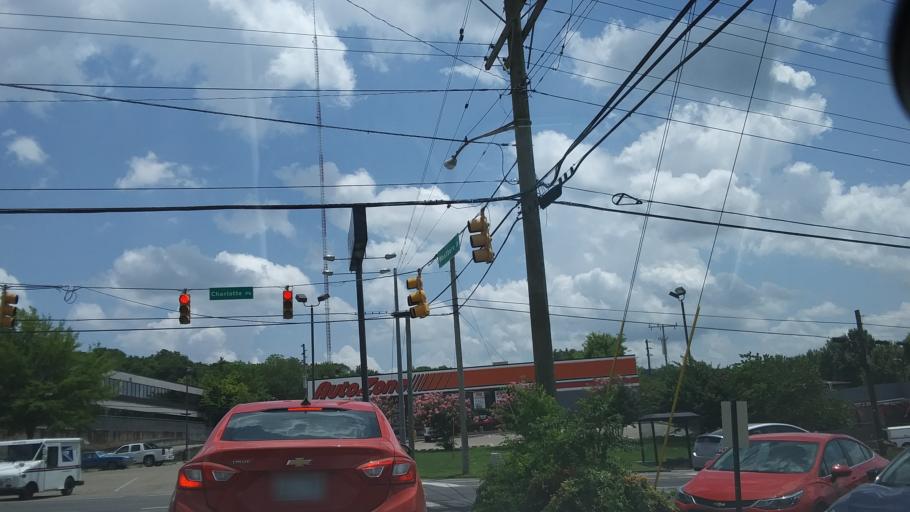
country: US
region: Tennessee
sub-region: Davidson County
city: Belle Meade
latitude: 36.1462
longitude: -86.8710
